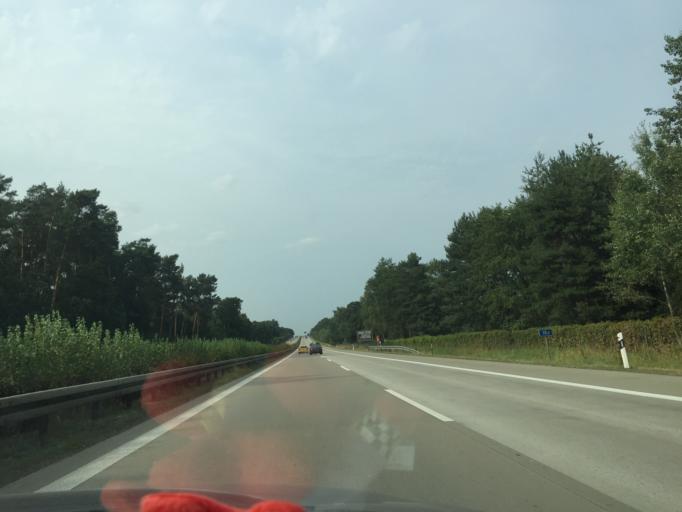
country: DE
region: Brandenburg
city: Bestensee
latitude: 52.2284
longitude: 13.5947
